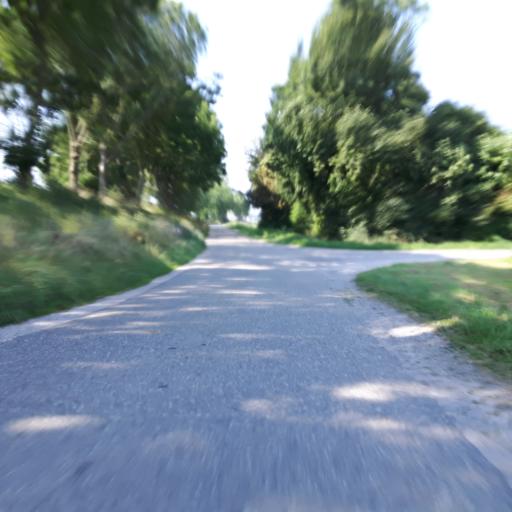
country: NL
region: Zeeland
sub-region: Gemeente Goes
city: Goes
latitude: 51.4595
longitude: 3.9266
